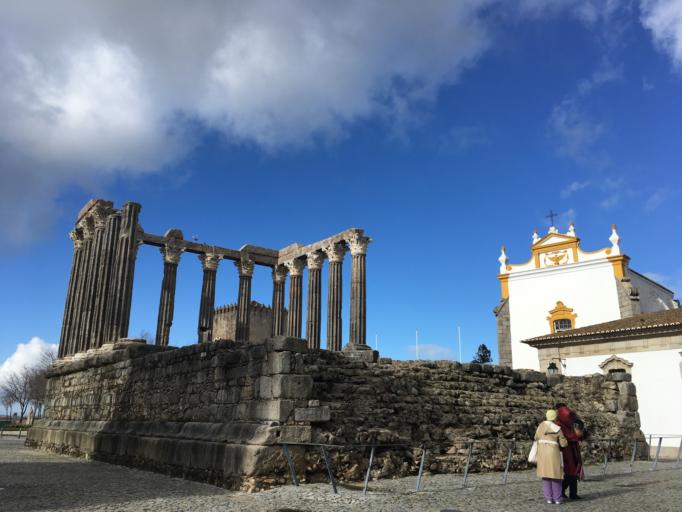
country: PT
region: Evora
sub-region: Evora
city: Evora
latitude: 38.5724
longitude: -7.9074
